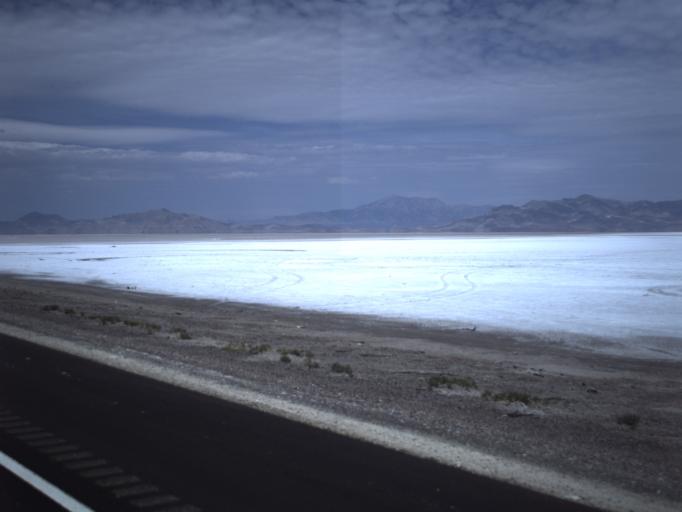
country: US
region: Utah
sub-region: Tooele County
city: Wendover
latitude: 40.7355
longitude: -113.6633
